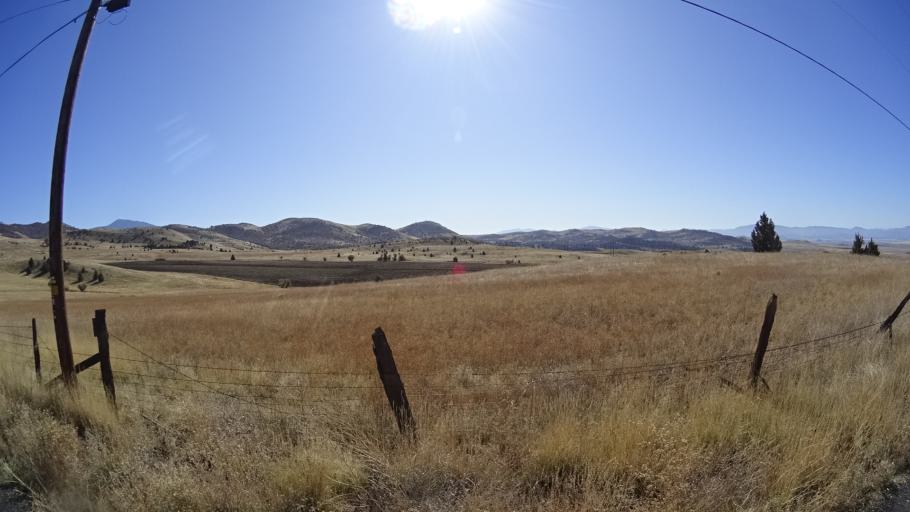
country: US
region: California
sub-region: Siskiyou County
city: Montague
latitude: 41.8300
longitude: -122.3598
